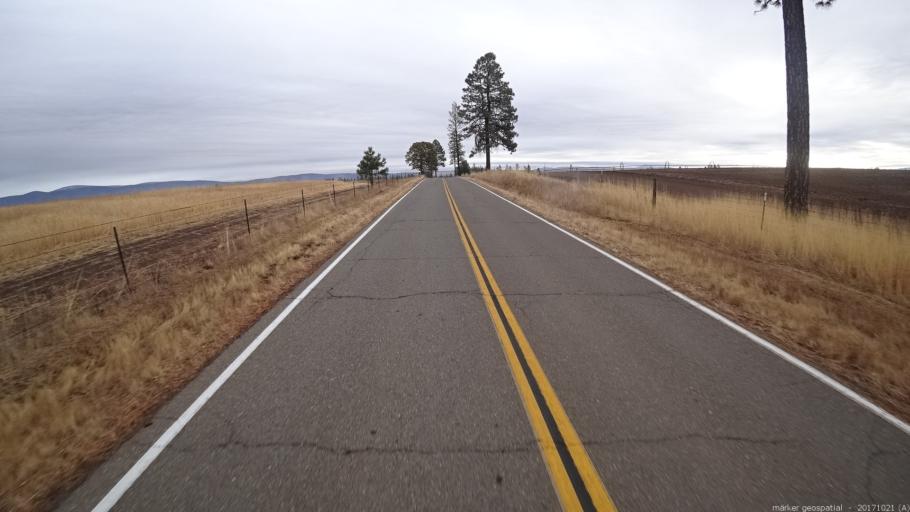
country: US
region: California
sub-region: Shasta County
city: Burney
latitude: 41.0253
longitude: -121.4032
